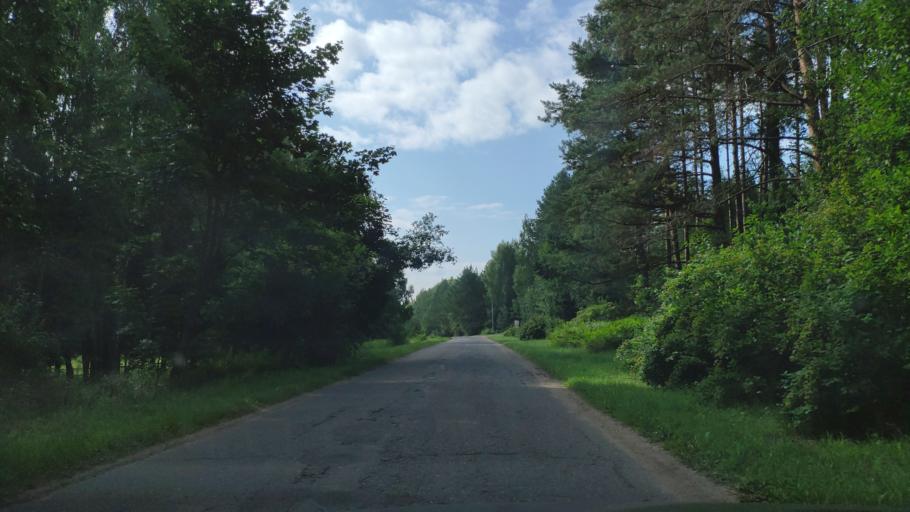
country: BY
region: Minsk
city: Zaslawye
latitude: 53.9826
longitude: 27.2891
